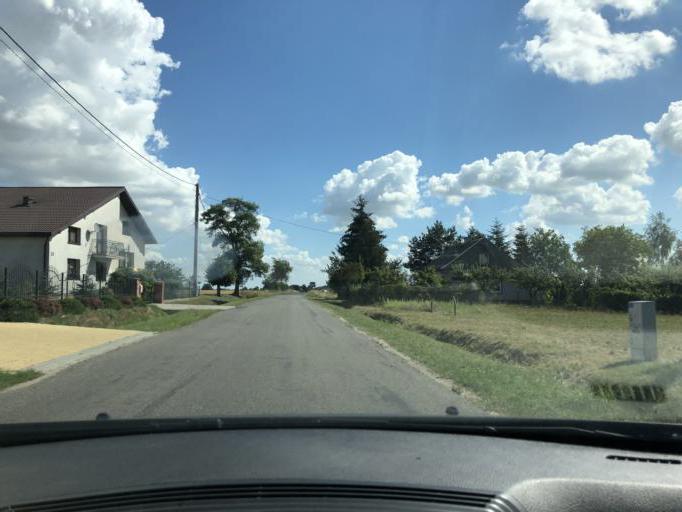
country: PL
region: Lodz Voivodeship
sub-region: Powiat wieruszowski
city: Walichnowy
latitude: 51.2610
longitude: 18.3674
